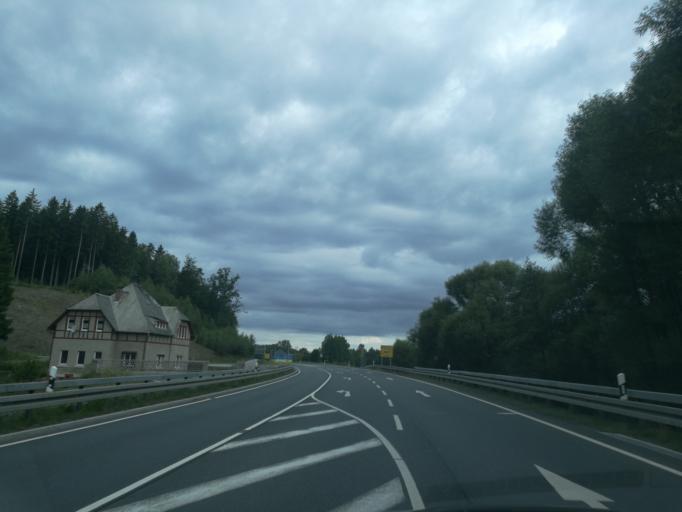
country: DE
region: Saxony
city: Adorf
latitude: 50.3413
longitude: 12.2467
